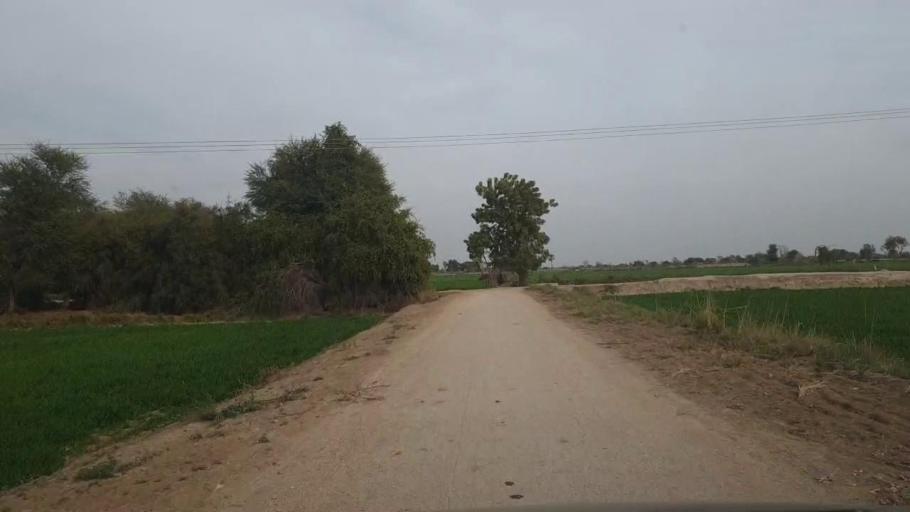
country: PK
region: Sindh
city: Shahpur Chakar
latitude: 26.1169
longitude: 68.5246
